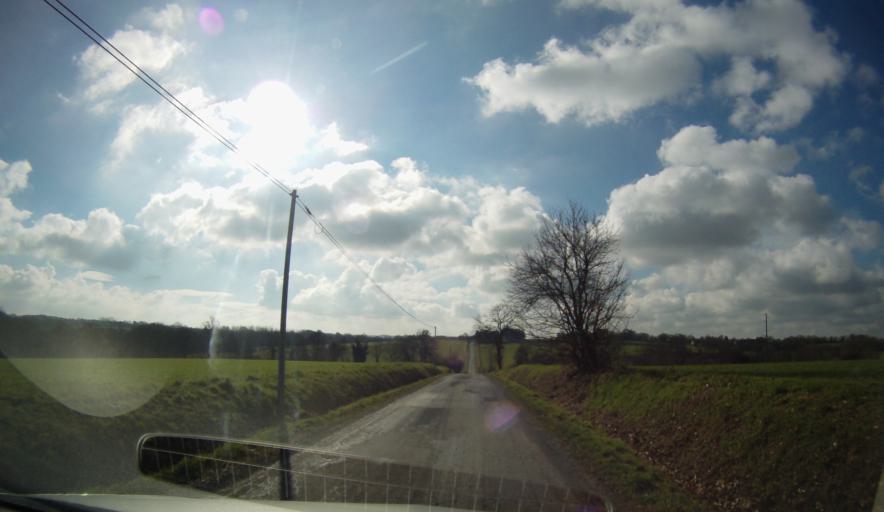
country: FR
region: Brittany
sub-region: Departement d'Ille-et-Vilaine
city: Corps-Nuds
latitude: 47.9668
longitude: -1.5914
